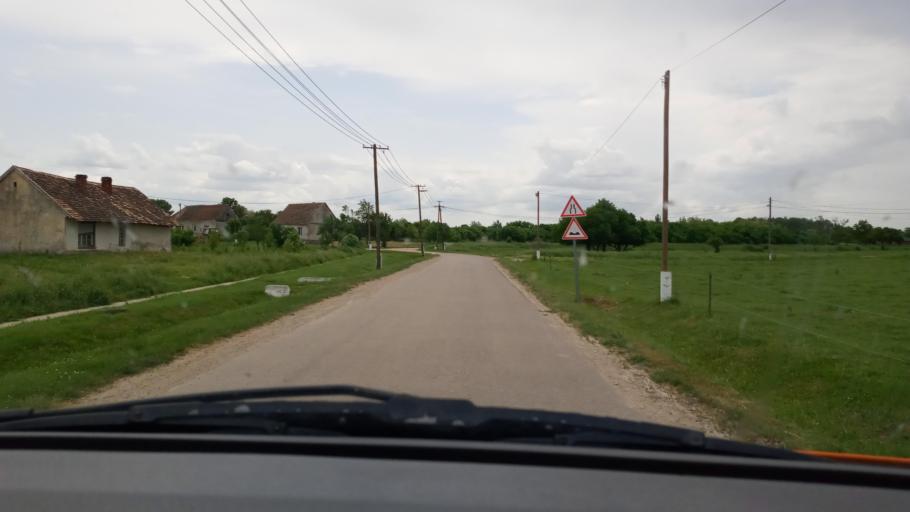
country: HU
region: Baranya
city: Vajszlo
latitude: 45.8225
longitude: 17.9935
